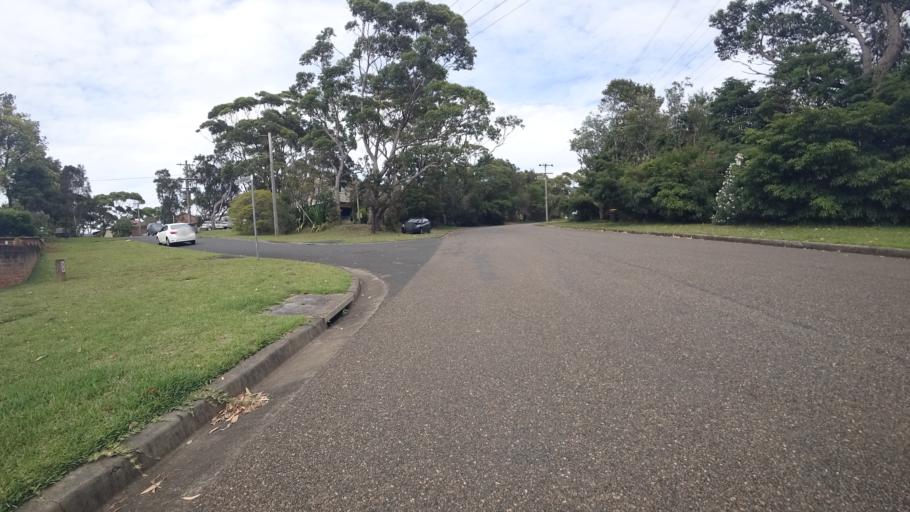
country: AU
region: New South Wales
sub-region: Shoalhaven Shire
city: Milton
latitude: -35.2557
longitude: 150.5213
